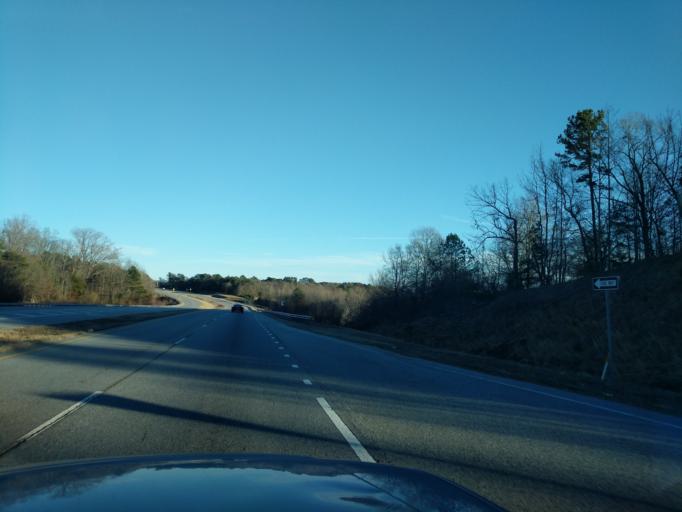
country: US
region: Georgia
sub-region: Stephens County
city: Toccoa
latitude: 34.5339
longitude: -83.3364
